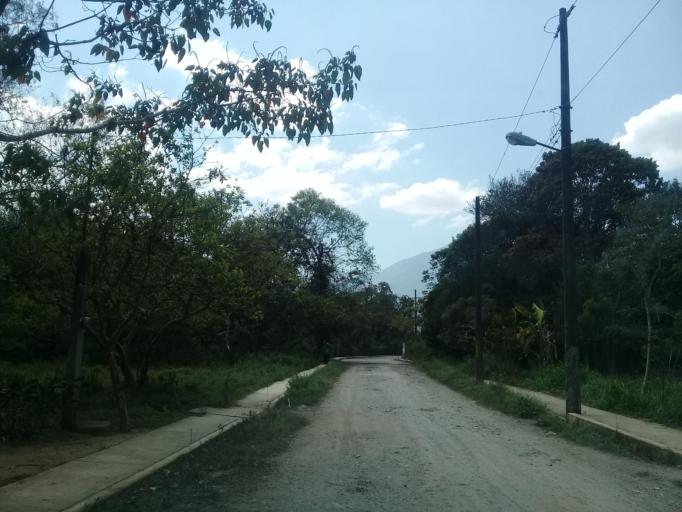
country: MX
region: Veracruz
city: Jalapilla
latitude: 18.8166
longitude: -97.0635
